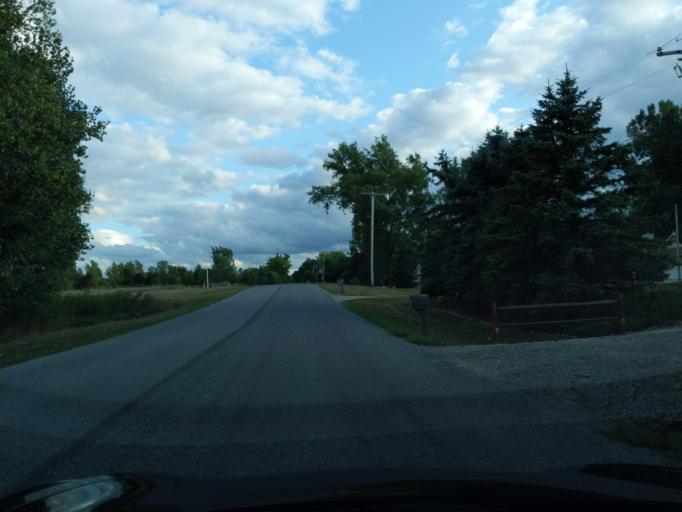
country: US
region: Michigan
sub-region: Eaton County
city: Dimondale
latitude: 42.6365
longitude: -84.5825
